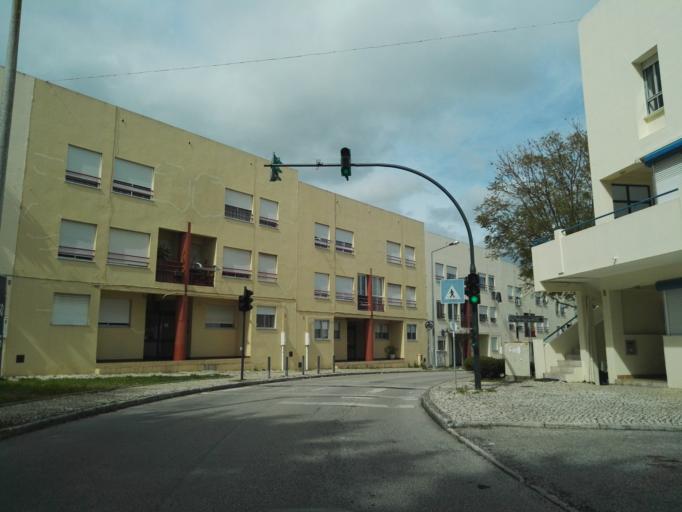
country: PT
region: Lisbon
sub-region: Vila Franca de Xira
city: Sobralinho
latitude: 38.8944
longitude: -9.0442
